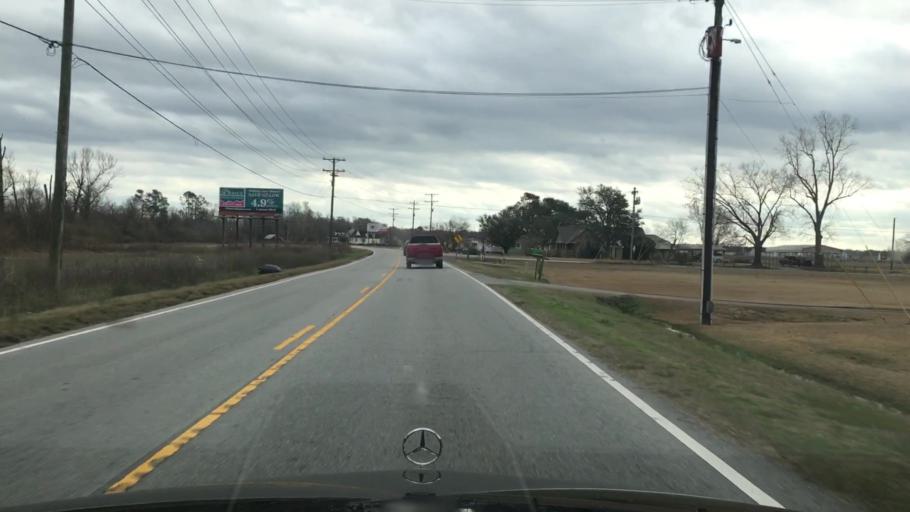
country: US
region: North Carolina
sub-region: Onslow County
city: Half Moon
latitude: 34.8482
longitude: -77.4808
